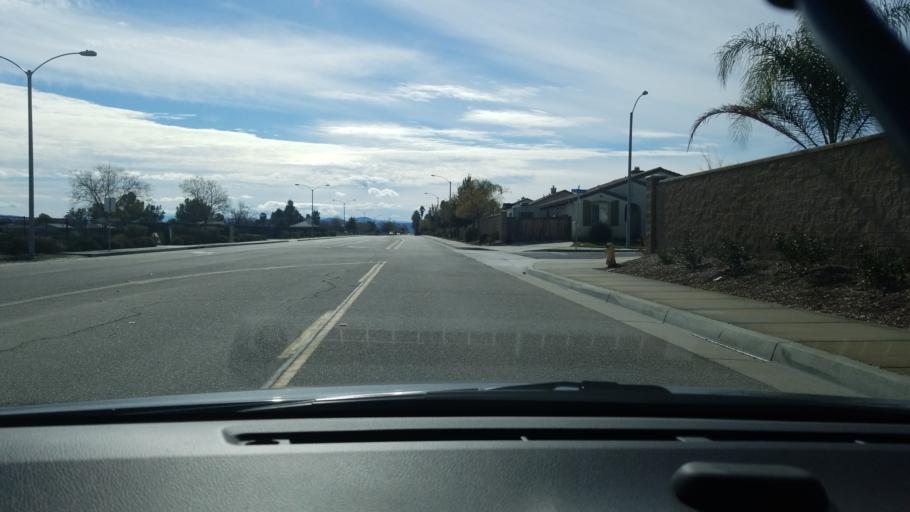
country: US
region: California
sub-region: Riverside County
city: Hemet
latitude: 33.7840
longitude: -117.0155
